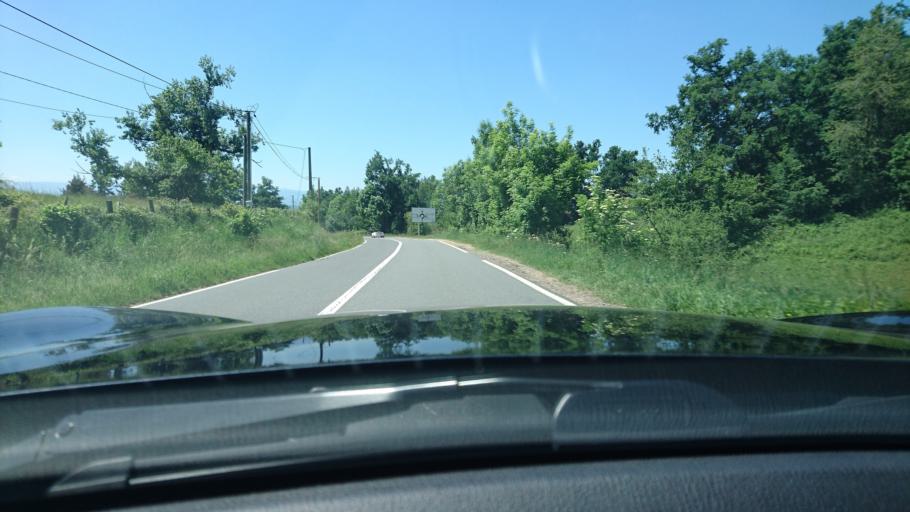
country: FR
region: Rhone-Alpes
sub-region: Departement de la Loire
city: Civens
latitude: 45.7793
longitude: 4.2579
